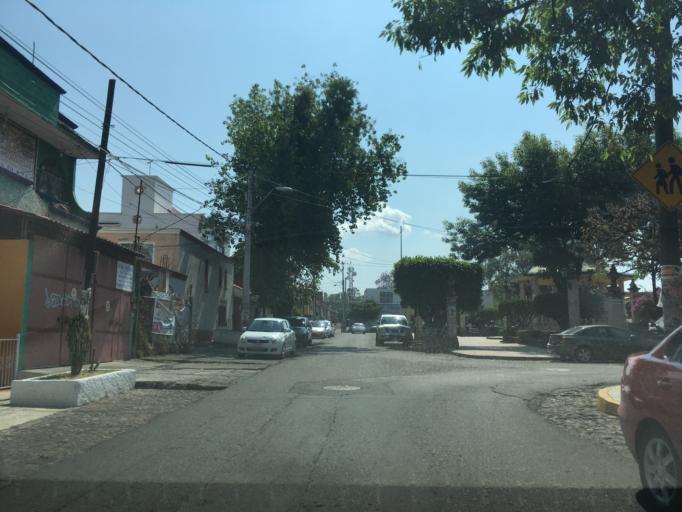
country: MX
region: Michoacan
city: Morelia
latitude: 19.6744
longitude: -101.1913
